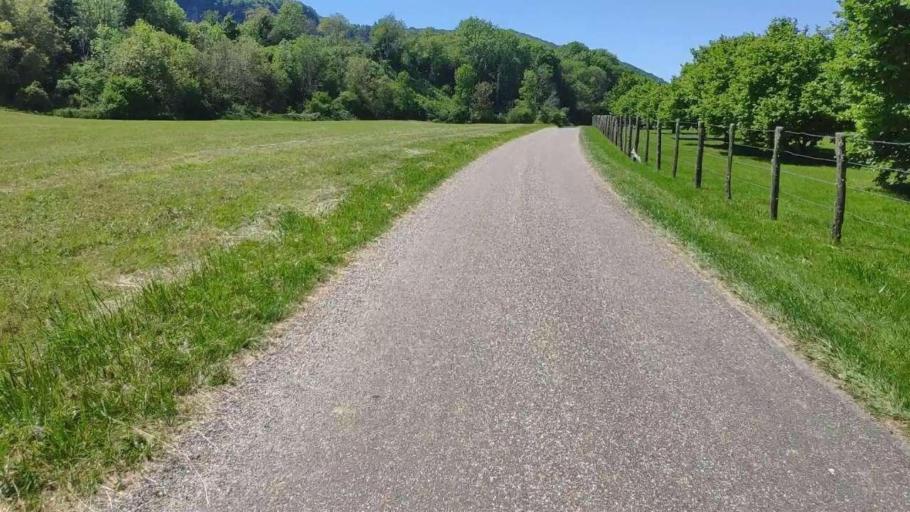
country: FR
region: Franche-Comte
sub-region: Departement du Jura
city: Perrigny
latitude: 46.7339
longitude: 5.6422
